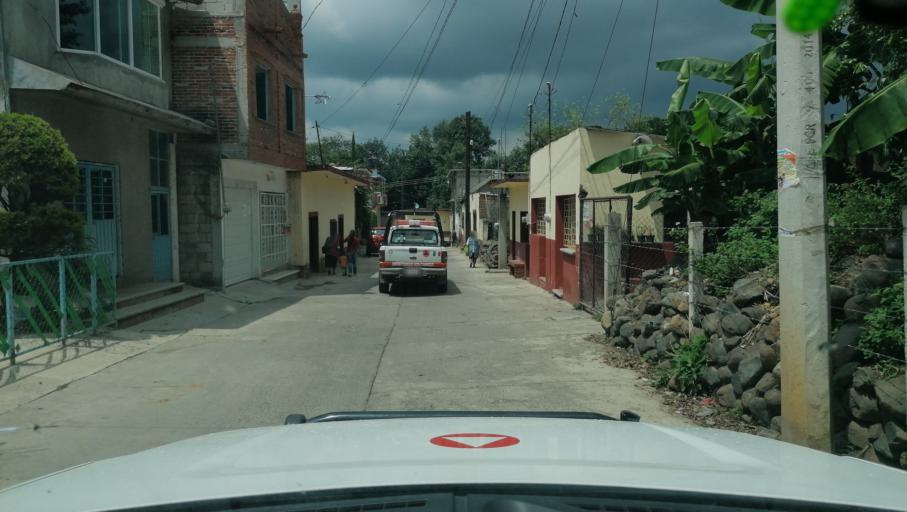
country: MX
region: Morelos
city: Ocuituco
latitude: 18.8832
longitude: -98.8187
